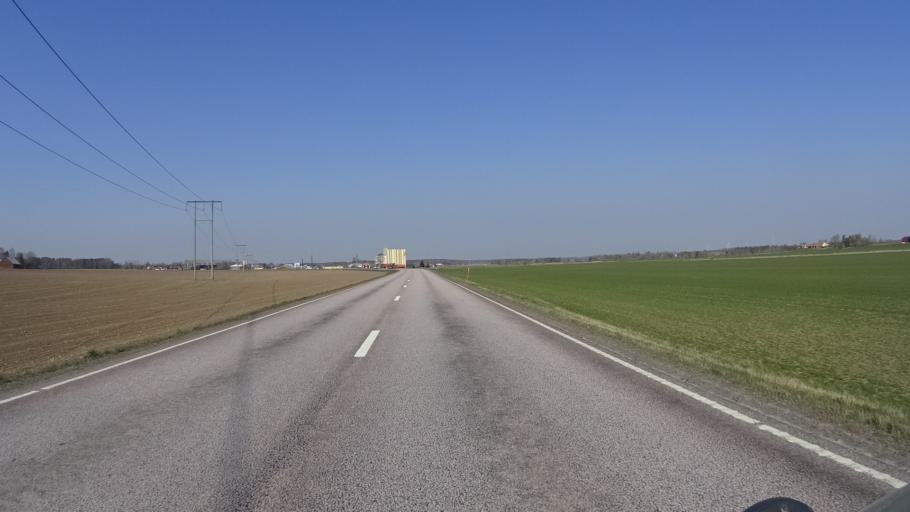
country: SE
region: OEstergoetland
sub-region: Mjolby Kommun
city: Mjolby
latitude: 58.3895
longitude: 15.1234
